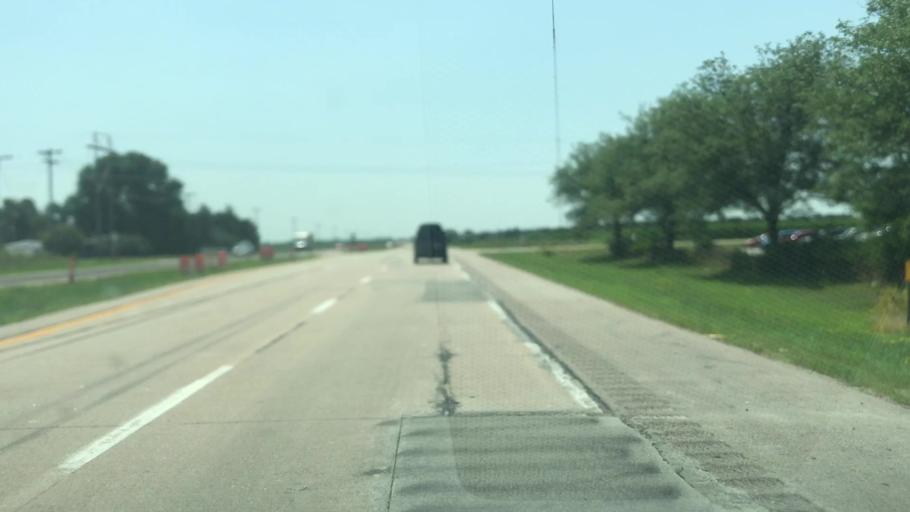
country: US
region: Nebraska
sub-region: Adams County
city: Hastings
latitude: 40.6561
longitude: -98.3825
